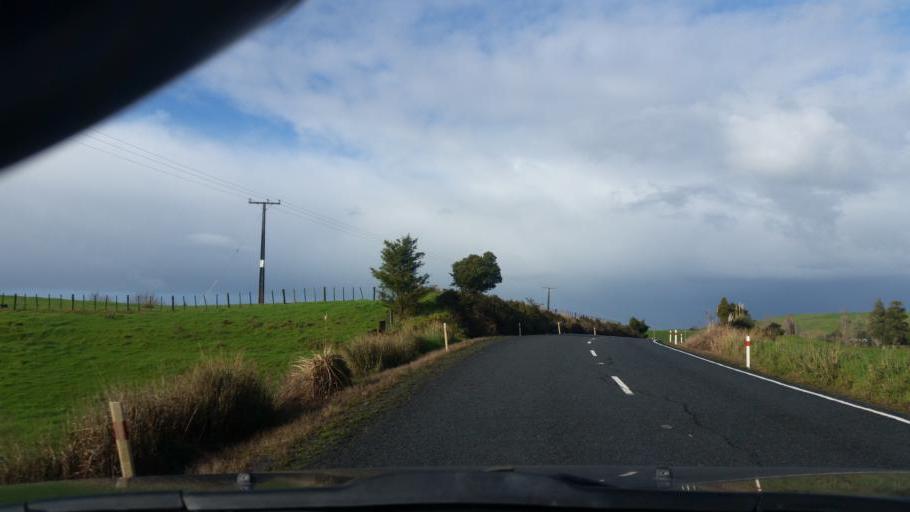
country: NZ
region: Northland
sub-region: Kaipara District
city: Dargaville
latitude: -35.8154
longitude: 173.9255
